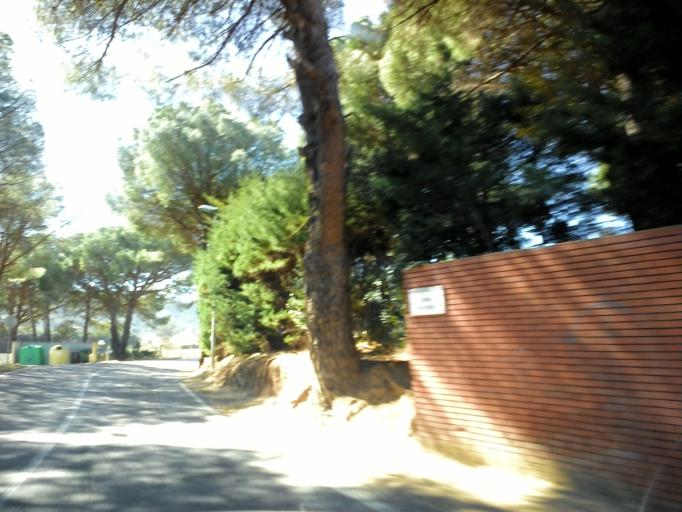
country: ES
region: Catalonia
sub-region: Provincia de Girona
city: Calonge
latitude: 41.8583
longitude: 3.0647
